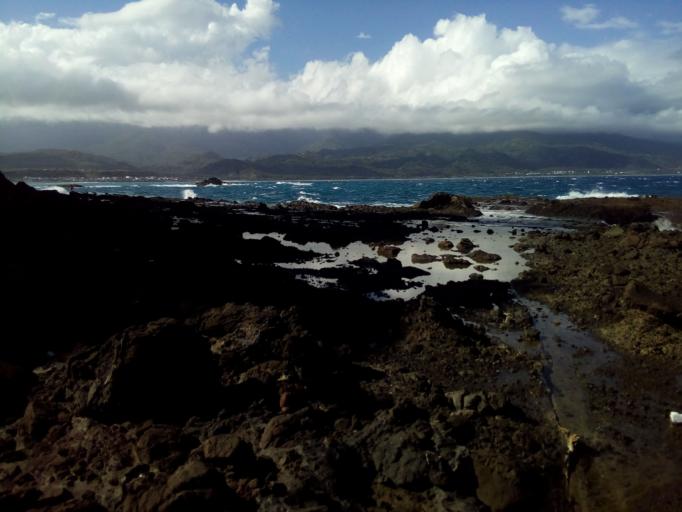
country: TW
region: Taiwan
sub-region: Taitung
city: Taitung
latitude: 23.1268
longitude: 121.4223
